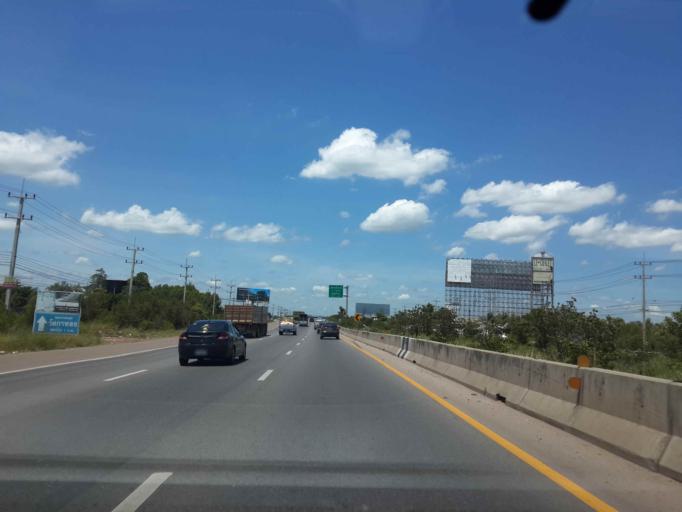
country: TH
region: Samut Sakhon
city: Ban Phaeo
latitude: 13.4778
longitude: 100.1179
